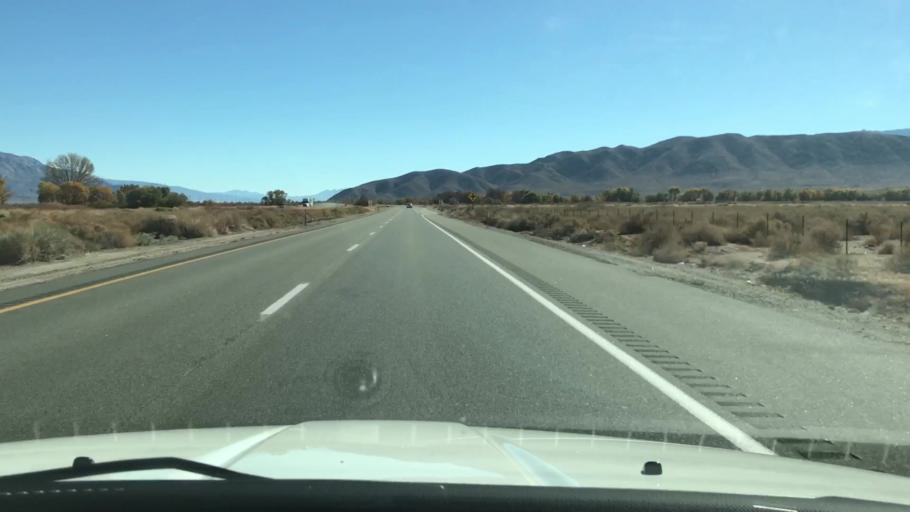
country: US
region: California
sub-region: Inyo County
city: Lone Pine
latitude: 36.7110
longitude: -118.1331
